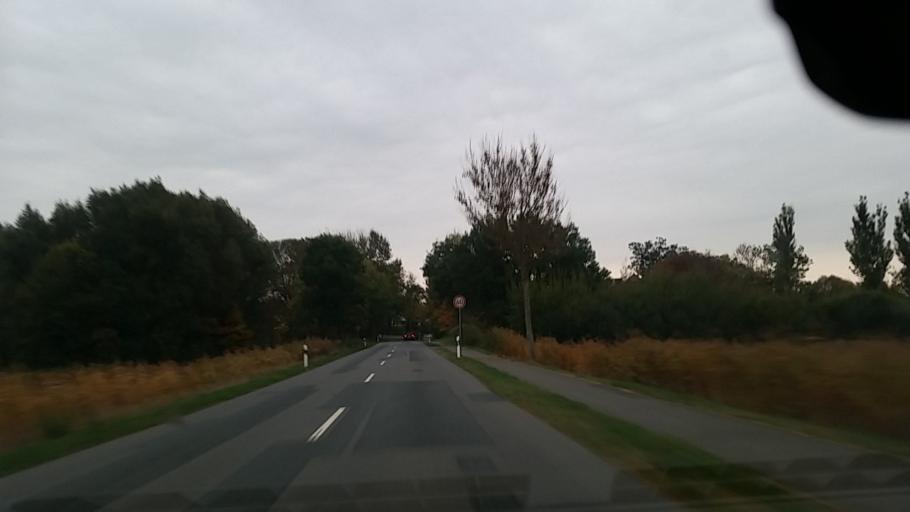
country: DE
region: Lower Saxony
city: Jembke
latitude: 52.4866
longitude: 10.7689
